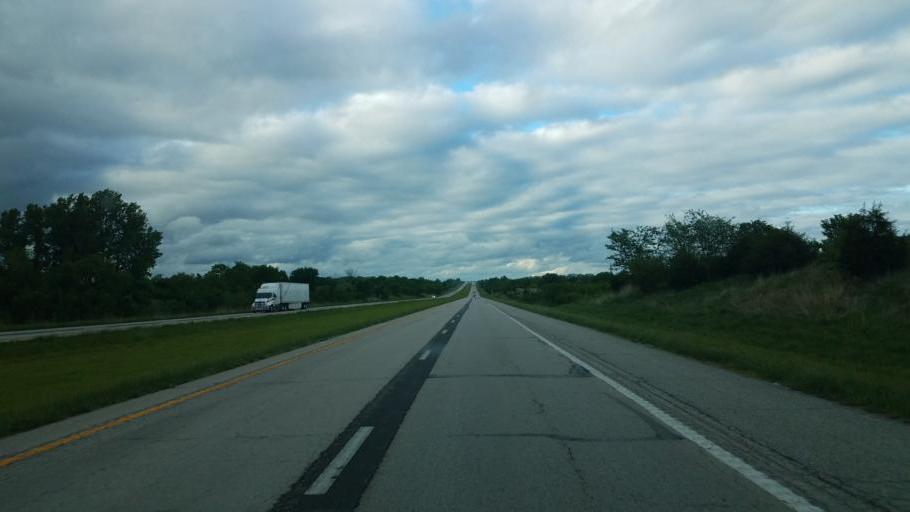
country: US
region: Missouri
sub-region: Harrison County
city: Bethany
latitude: 40.3975
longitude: -93.9963
